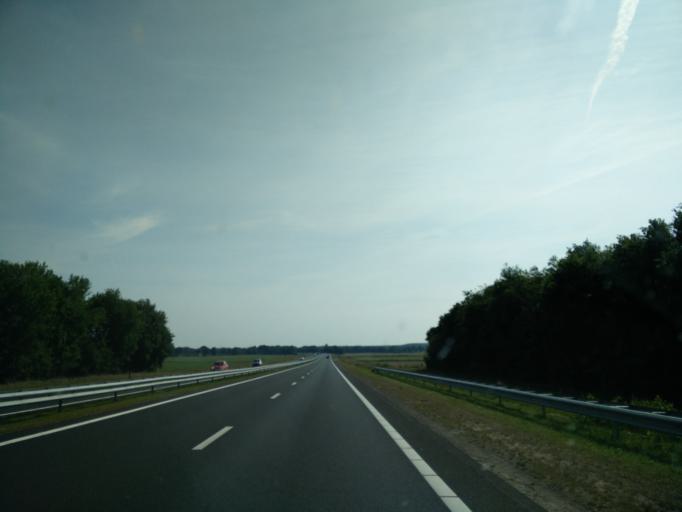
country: NL
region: Drenthe
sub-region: Gemeente Aa en Hunze
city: Anloo
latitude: 52.9809
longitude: 6.6692
